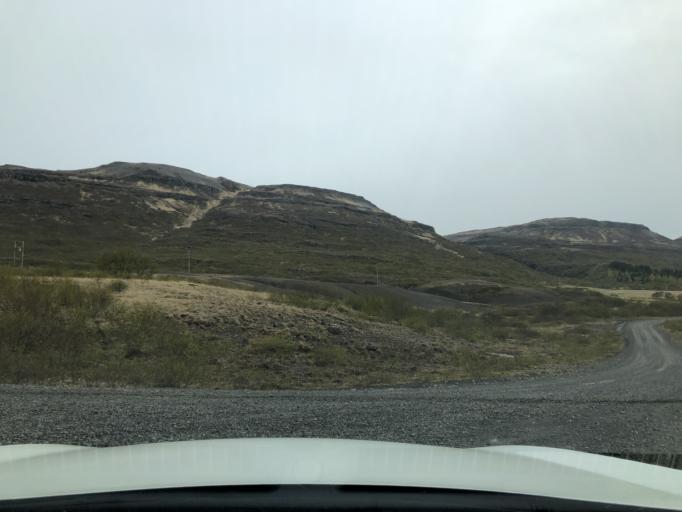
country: IS
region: South
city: Hveragerdi
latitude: 64.3846
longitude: -21.3412
